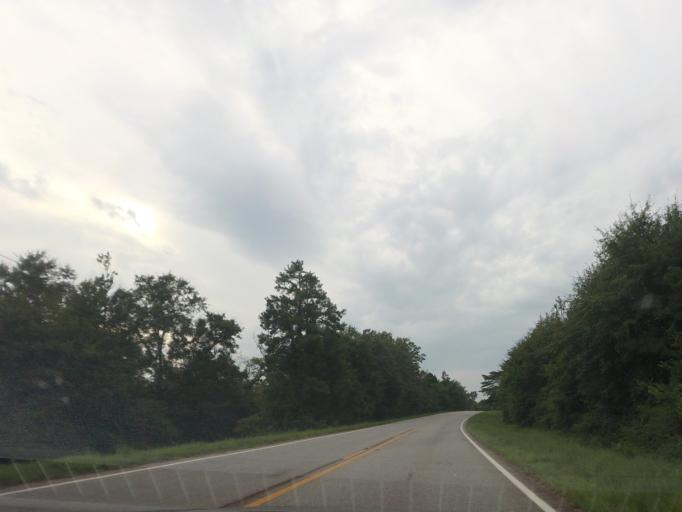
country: US
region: Georgia
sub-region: Twiggs County
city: Jeffersonville
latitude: 32.7219
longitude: -83.4145
